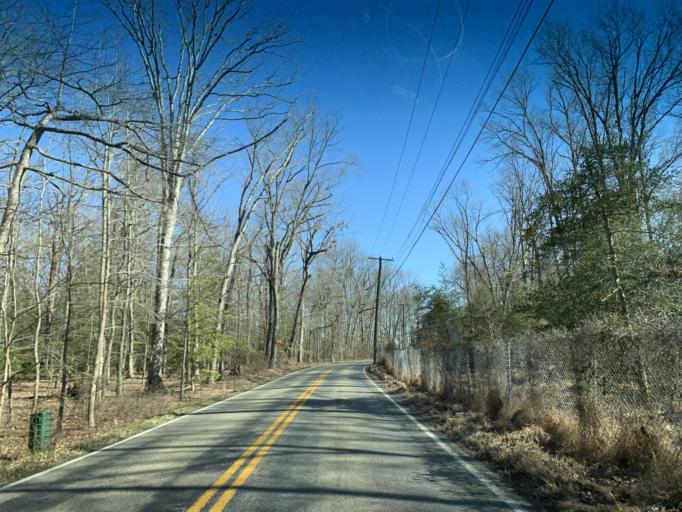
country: US
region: Maryland
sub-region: Cecil County
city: North East
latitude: 39.4947
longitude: -75.8841
